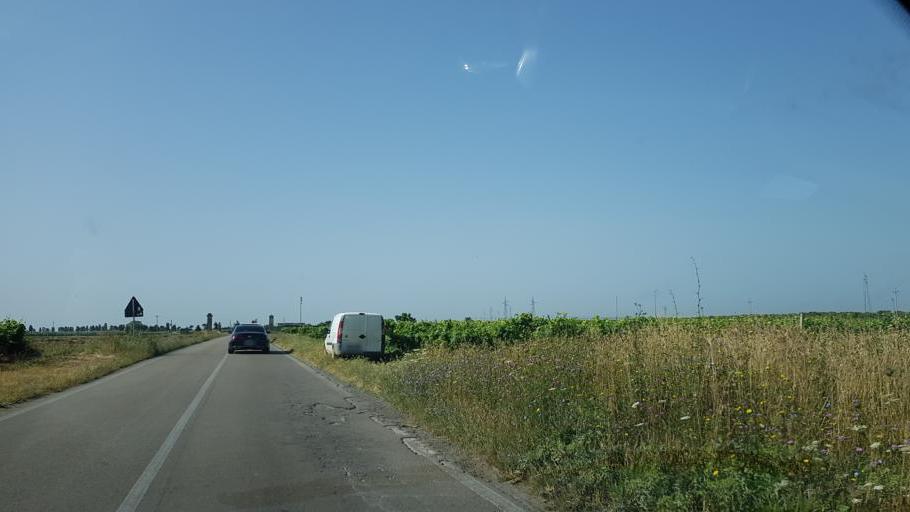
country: IT
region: Apulia
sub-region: Provincia di Brindisi
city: San Pancrazio Salentino
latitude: 40.3946
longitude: 17.8347
